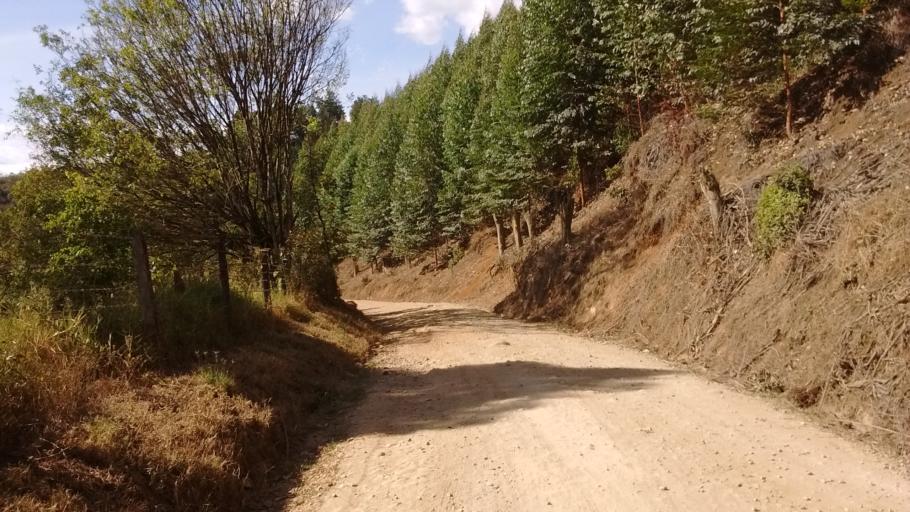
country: CO
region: Cauca
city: Popayan
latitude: 2.4641
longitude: -76.5755
